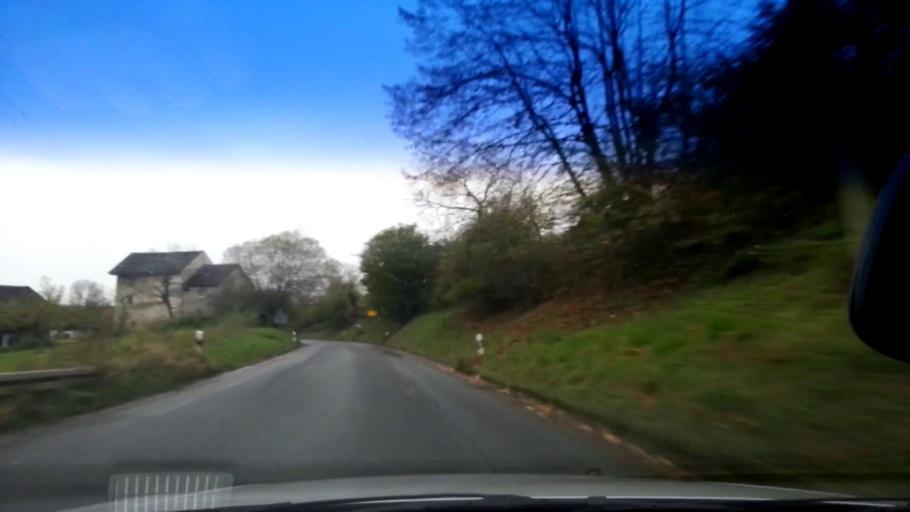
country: DE
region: Bavaria
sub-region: Upper Franconia
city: Wattendorf
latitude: 50.0135
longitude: 11.0759
